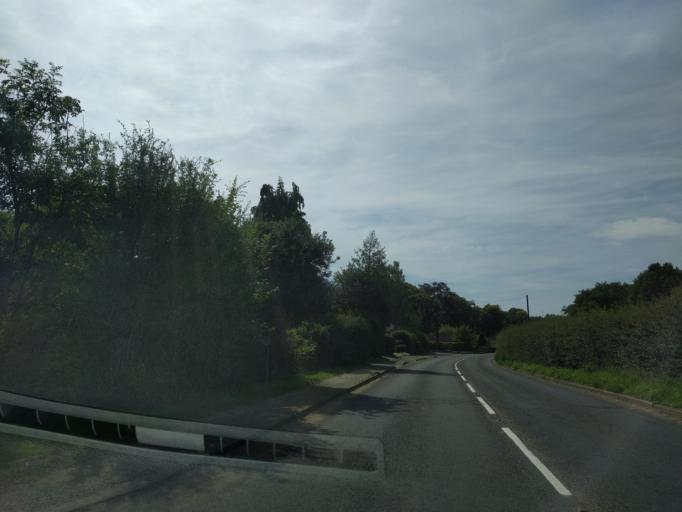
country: GB
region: England
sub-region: Surrey
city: Chilworth
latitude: 51.2164
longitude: -0.5186
